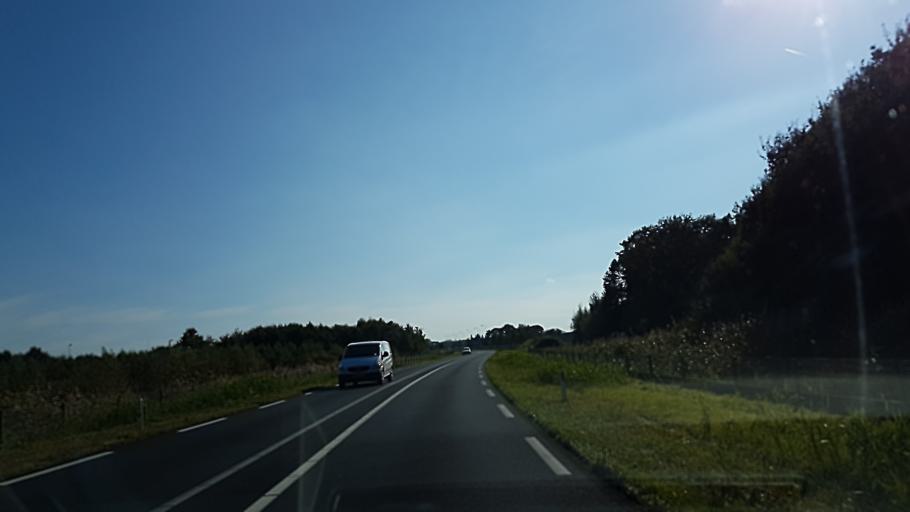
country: NL
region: North Brabant
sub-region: Gemeente Woensdrecht
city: Woensdrecht
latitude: 51.4333
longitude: 4.3402
